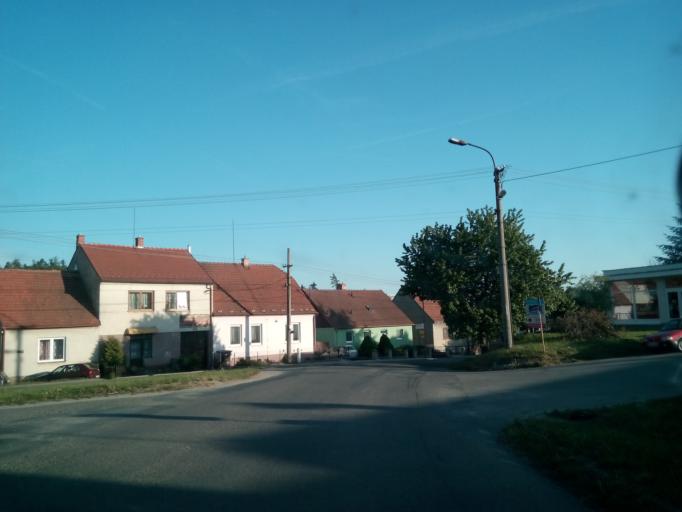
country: CZ
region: South Moravian
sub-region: Okres Blansko
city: Jedovnice
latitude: 49.3474
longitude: 16.7610
